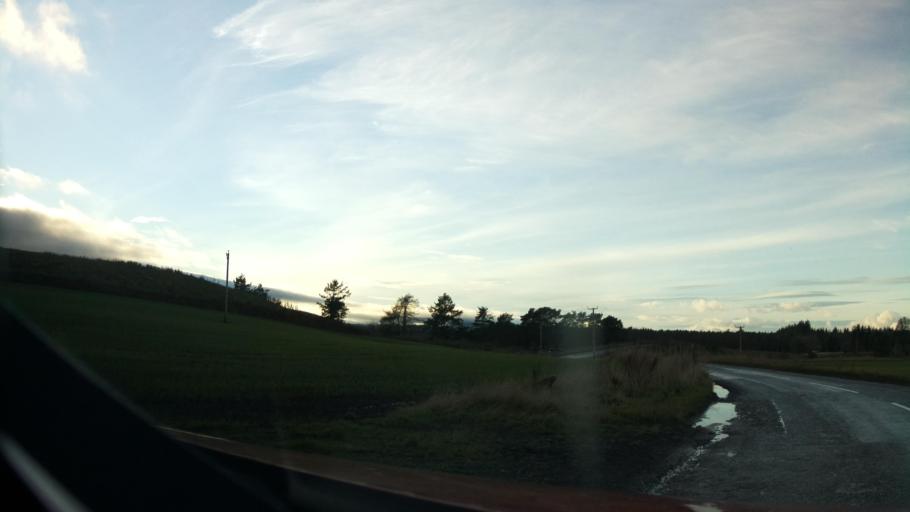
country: GB
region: Scotland
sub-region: Angus
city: Letham
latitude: 56.5839
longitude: -2.8171
